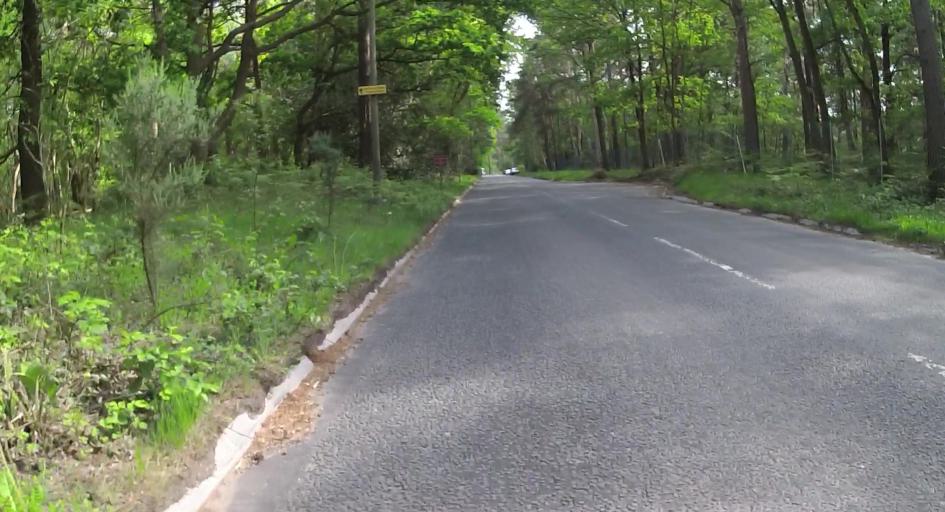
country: GB
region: England
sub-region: Hampshire
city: Fleet
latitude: 51.2893
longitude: -0.8037
